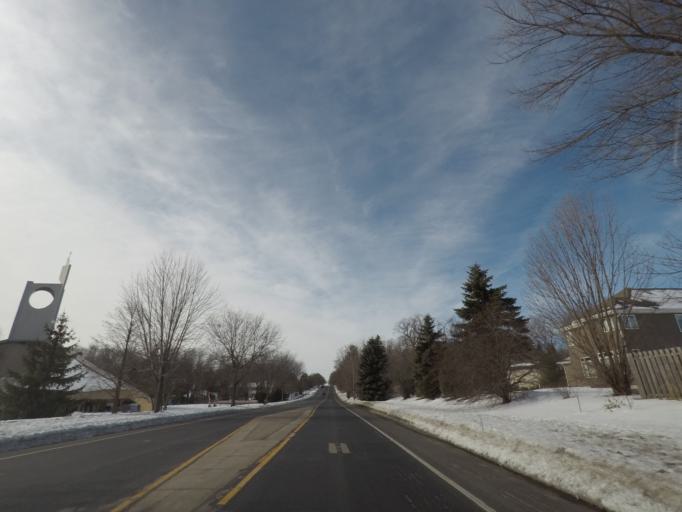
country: US
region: Wisconsin
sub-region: Dane County
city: Fitchburg
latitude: 43.0013
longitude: -89.4377
